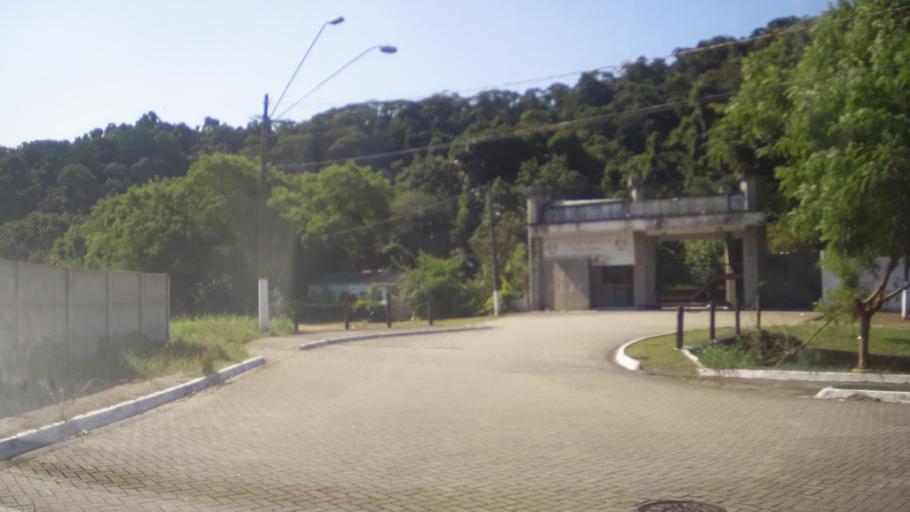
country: BR
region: Sao Paulo
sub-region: Praia Grande
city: Praia Grande
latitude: -24.0022
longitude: -46.4097
